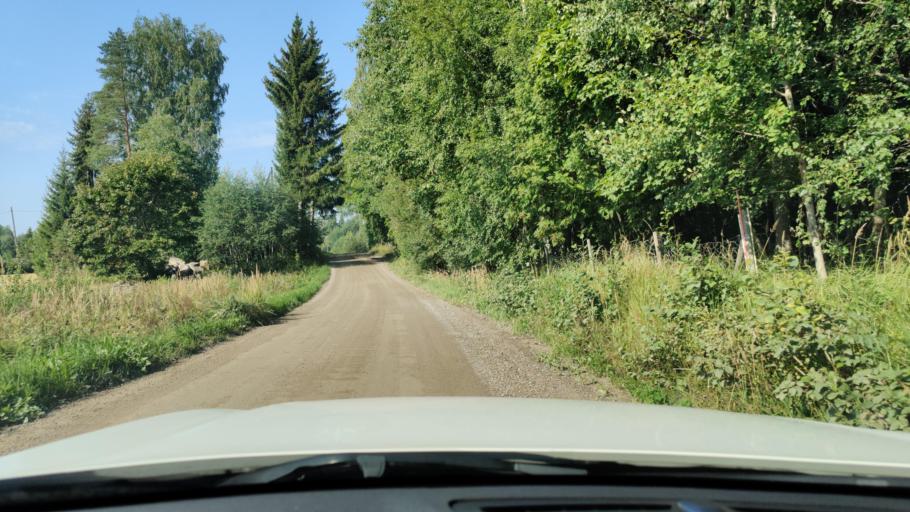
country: FI
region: Haeme
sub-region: Riihimaeki
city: Loppi
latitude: 60.6757
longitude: 24.5819
